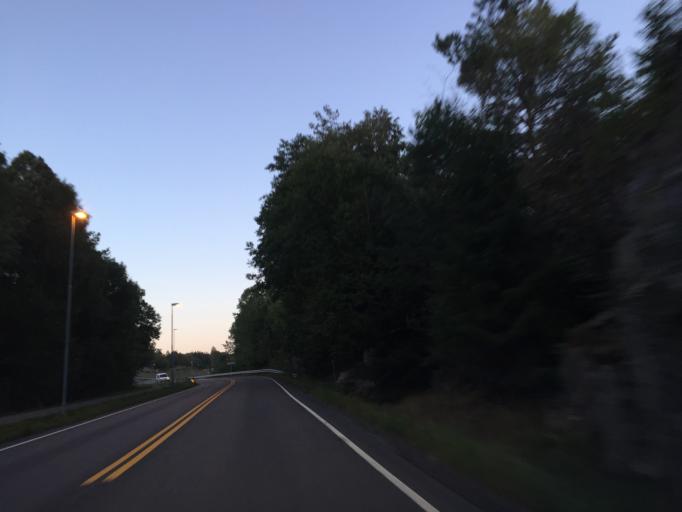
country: NO
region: Ostfold
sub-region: Moss
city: Moss
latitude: 59.5142
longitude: 10.6904
